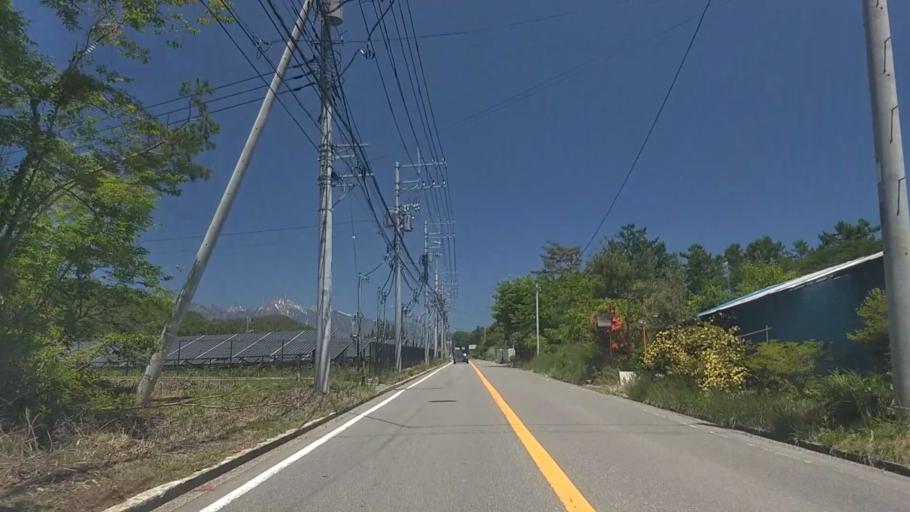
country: JP
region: Yamanashi
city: Nirasaki
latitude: 35.8494
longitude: 138.4323
